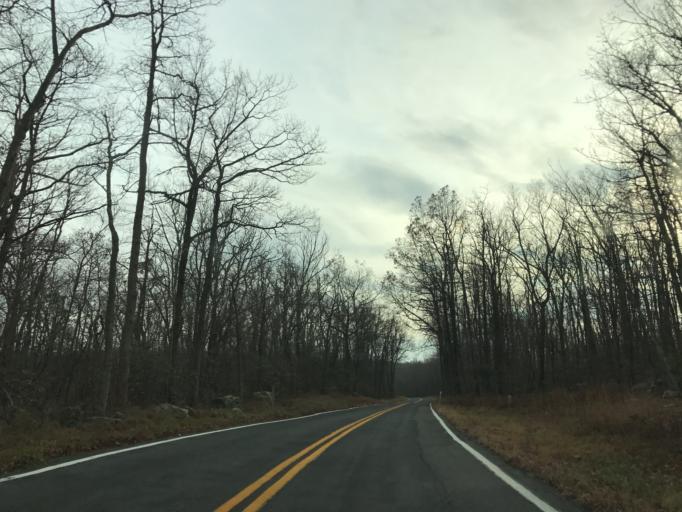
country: US
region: Maryland
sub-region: Frederick County
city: Myersville
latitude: 39.5433
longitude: -77.4995
